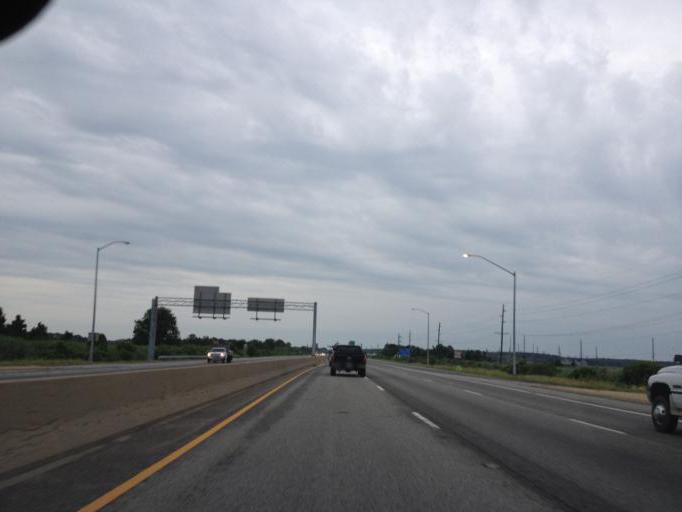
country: US
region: Maryland
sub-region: Queen Anne's County
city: Grasonville
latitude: 38.9683
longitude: -76.2376
